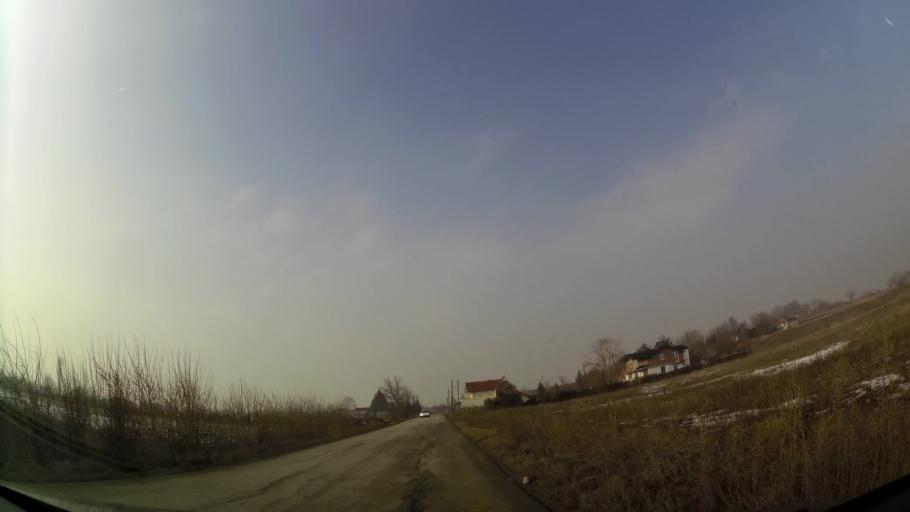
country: MK
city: Kadino
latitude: 41.9778
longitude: 21.6003
